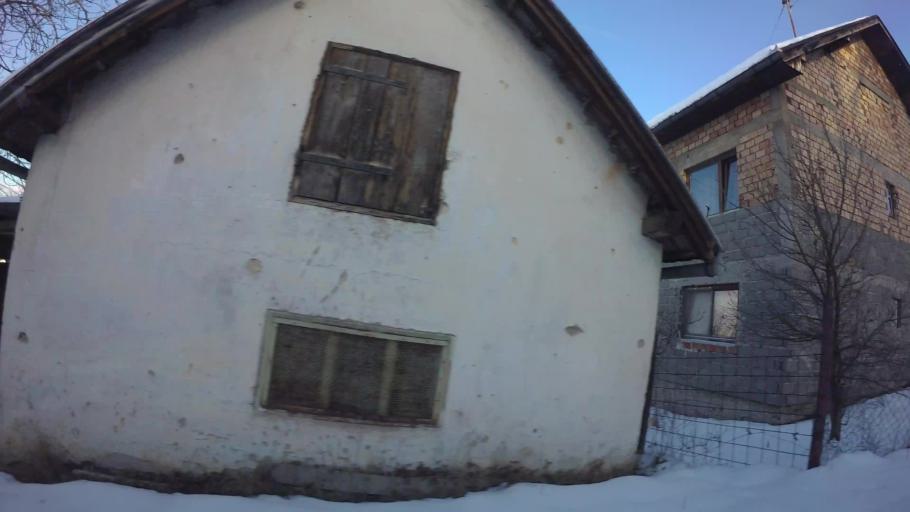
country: BA
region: Federation of Bosnia and Herzegovina
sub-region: Kanton Sarajevo
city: Sarajevo
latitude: 43.8085
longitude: 18.3519
